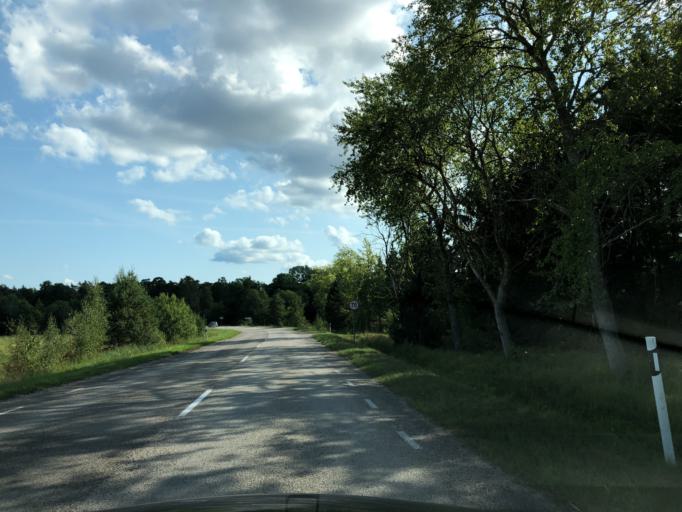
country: EE
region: Hiiumaa
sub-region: Kaerdla linn
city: Kardla
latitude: 58.7100
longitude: 22.5873
